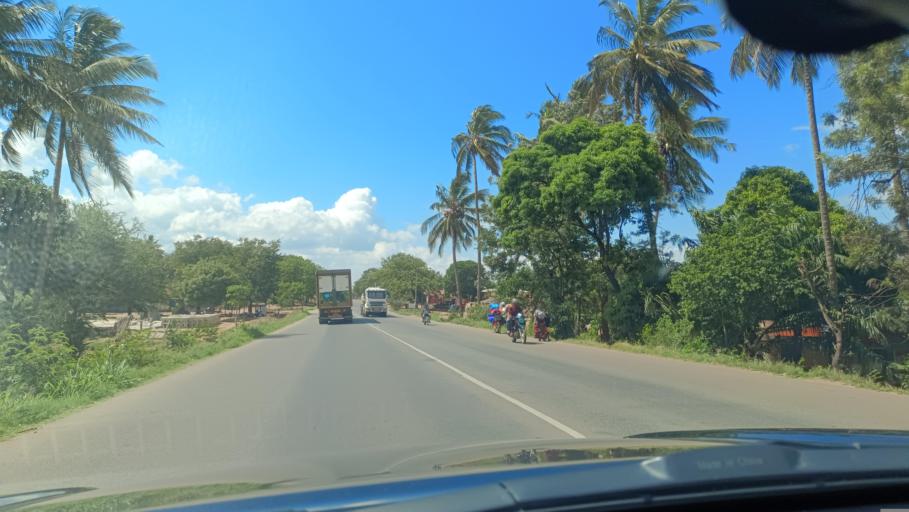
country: TZ
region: Morogoro
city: Morogoro
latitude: -6.8144
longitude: 37.6497
